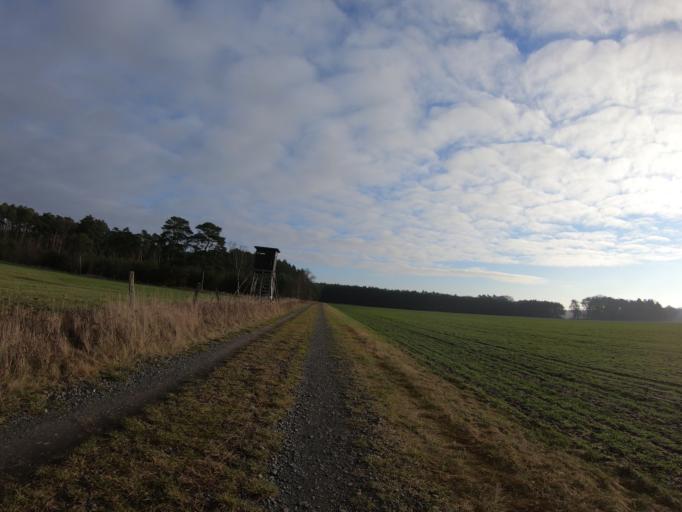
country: DE
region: Lower Saxony
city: Ribbesbuttel
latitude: 52.4798
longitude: 10.4880
